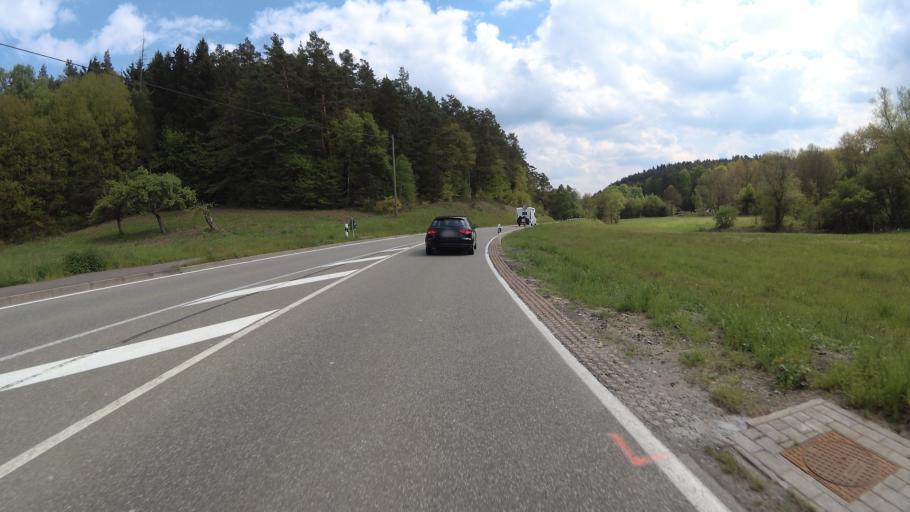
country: DE
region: Rheinland-Pfalz
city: Enkenbach-Alsenborn
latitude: 49.4721
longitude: 7.9148
